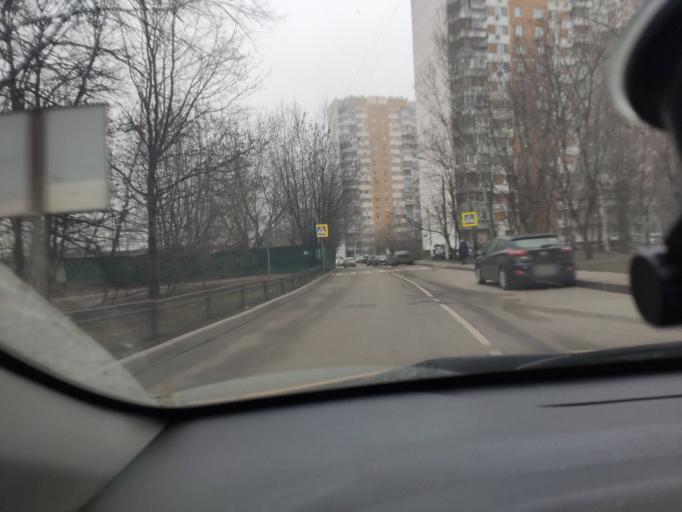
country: RU
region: Moscow
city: Chertanovo Yuzhnoye
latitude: 55.5934
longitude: 37.5943
